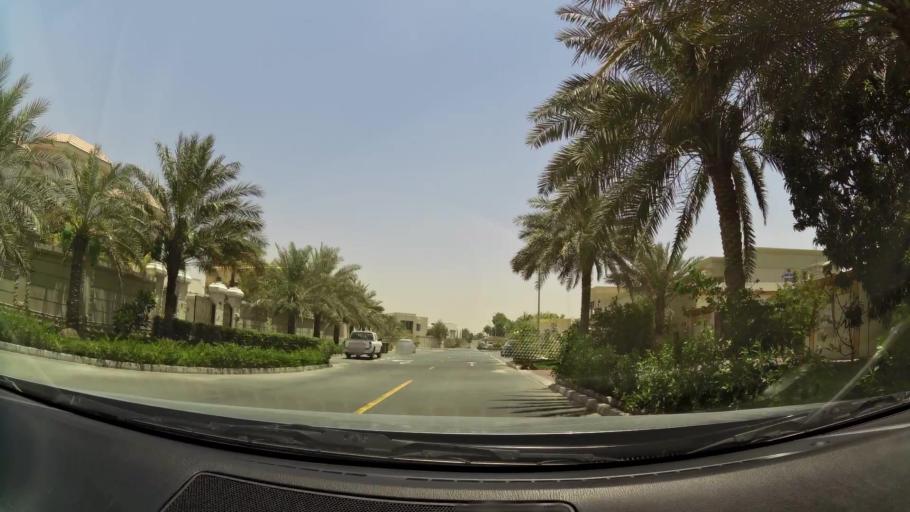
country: AE
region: Dubai
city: Dubai
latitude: 25.1014
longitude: 55.1953
